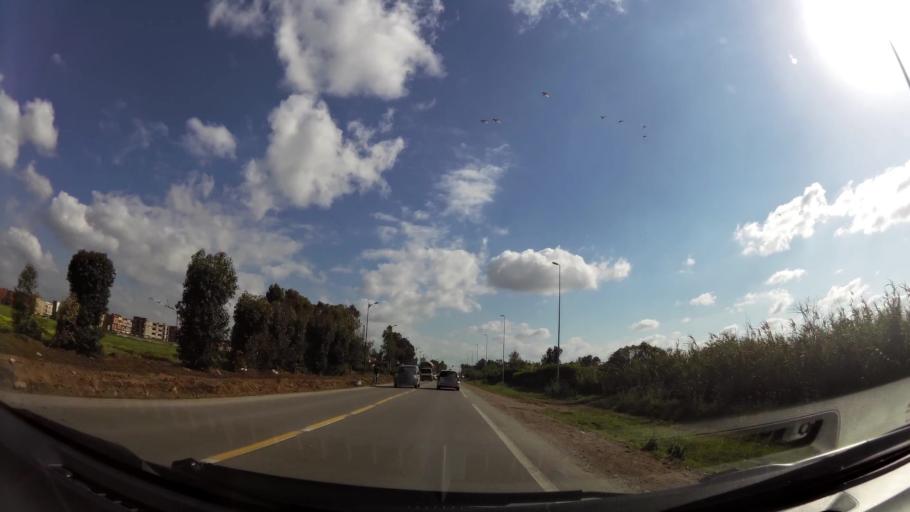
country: MA
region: Grand Casablanca
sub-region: Mediouna
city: Mediouna
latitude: 33.3785
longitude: -7.5408
